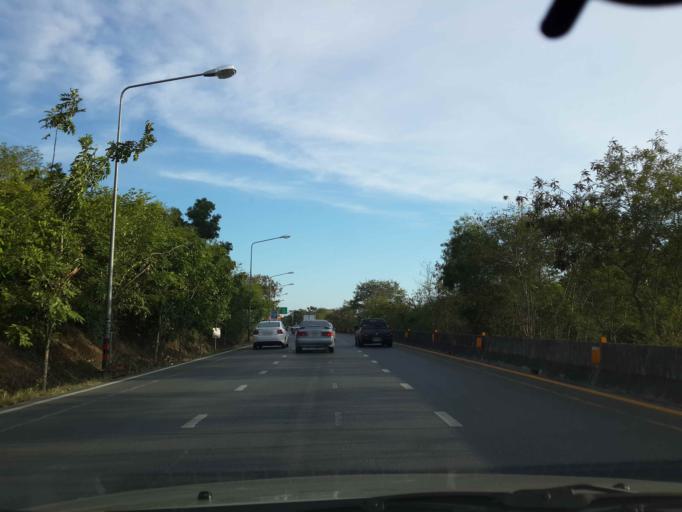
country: TH
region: Chon Buri
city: Phatthaya
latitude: 12.9291
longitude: 100.9043
